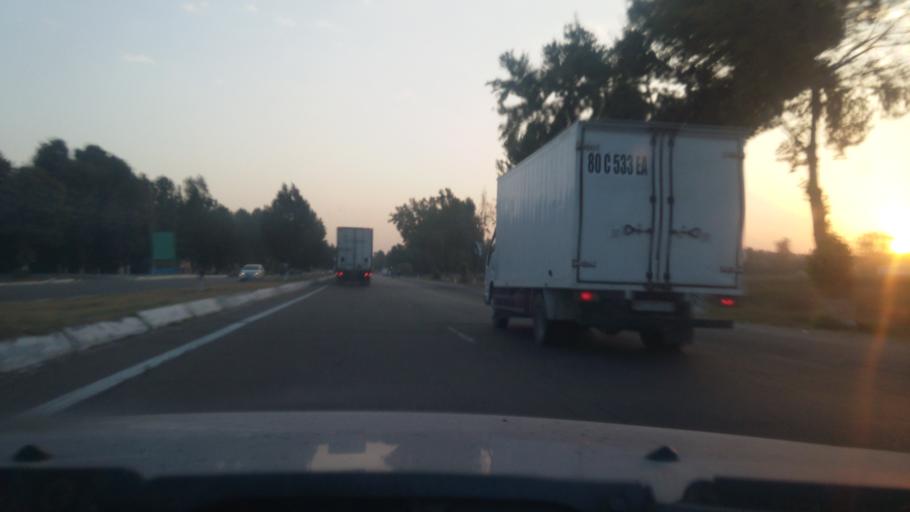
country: UZ
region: Toshkent
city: Zafar
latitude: 41.0374
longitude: 68.8768
